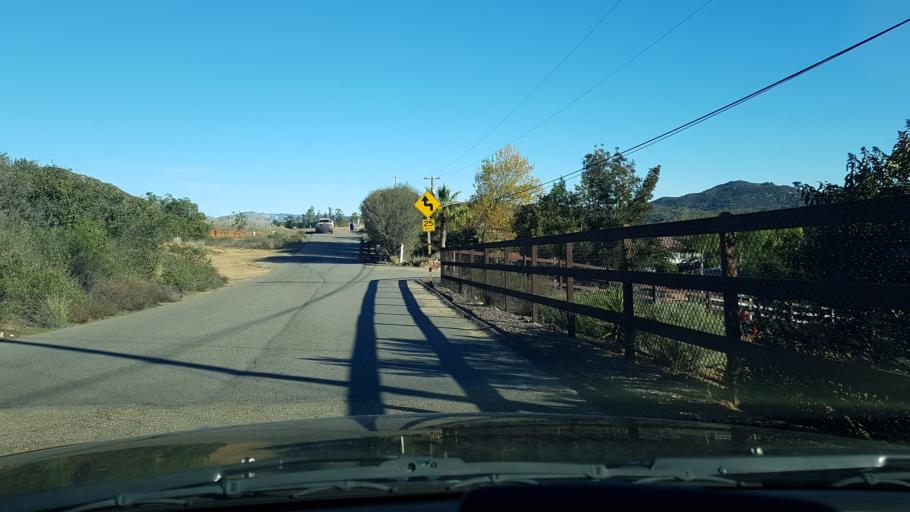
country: US
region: California
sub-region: San Diego County
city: Hidden Meadows
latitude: 33.2172
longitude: -117.0932
